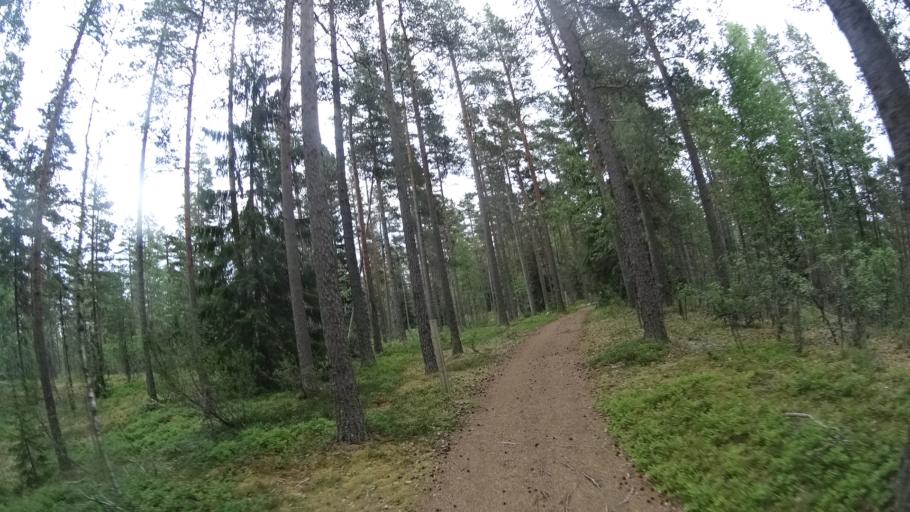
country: FI
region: Satakunta
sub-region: Pohjois-Satakunta
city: Jaemijaervi
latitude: 61.7721
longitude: 22.7362
